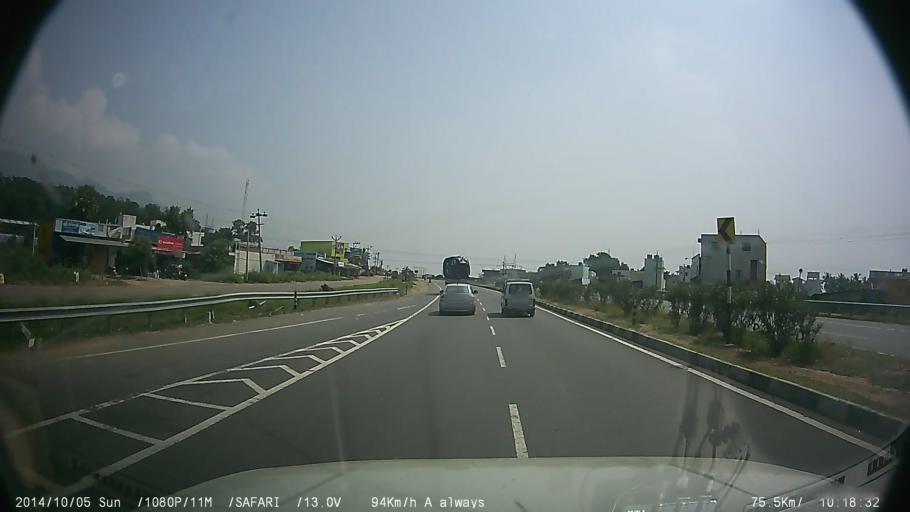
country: IN
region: Tamil Nadu
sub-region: Salem
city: Attayyampatti
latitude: 11.5824
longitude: 78.0552
